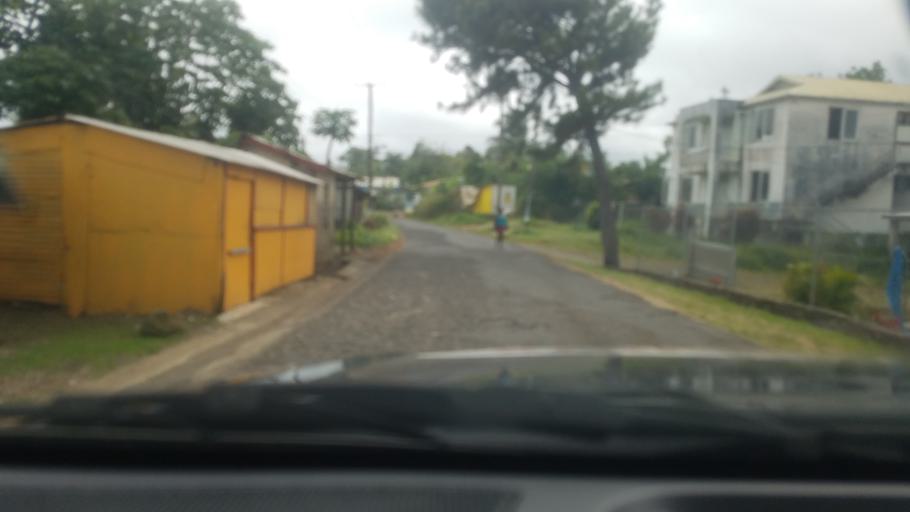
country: LC
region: Micoud Quarter
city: Micoud
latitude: 13.8055
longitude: -60.9455
